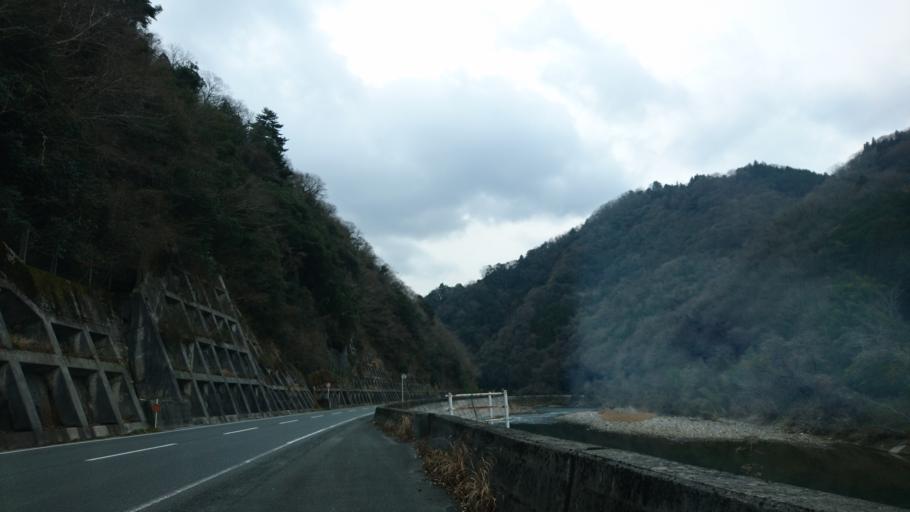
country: JP
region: Okayama
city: Niimi
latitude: 34.9180
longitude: 133.5242
